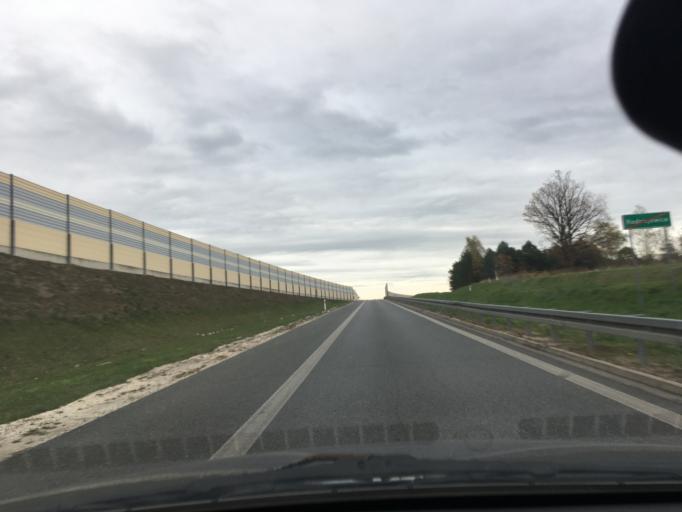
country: PL
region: Masovian Voivodeship
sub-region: Powiat zyrardowski
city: Radziejowice
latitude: 52.0021
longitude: 20.5611
